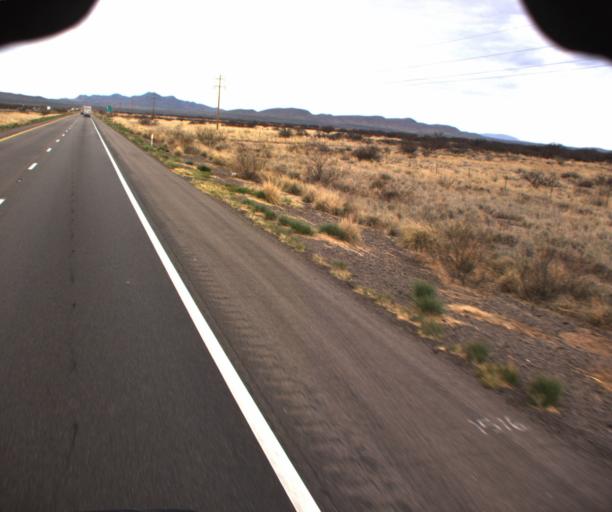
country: US
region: Arizona
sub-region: Cochise County
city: Willcox
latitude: 32.1992
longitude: -109.9116
